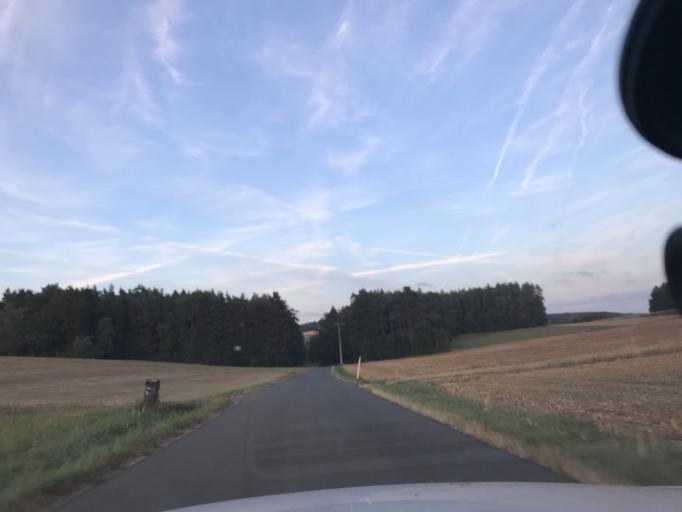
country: DE
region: Bavaria
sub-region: Upper Franconia
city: Pegnitz
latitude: 49.7376
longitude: 11.5895
